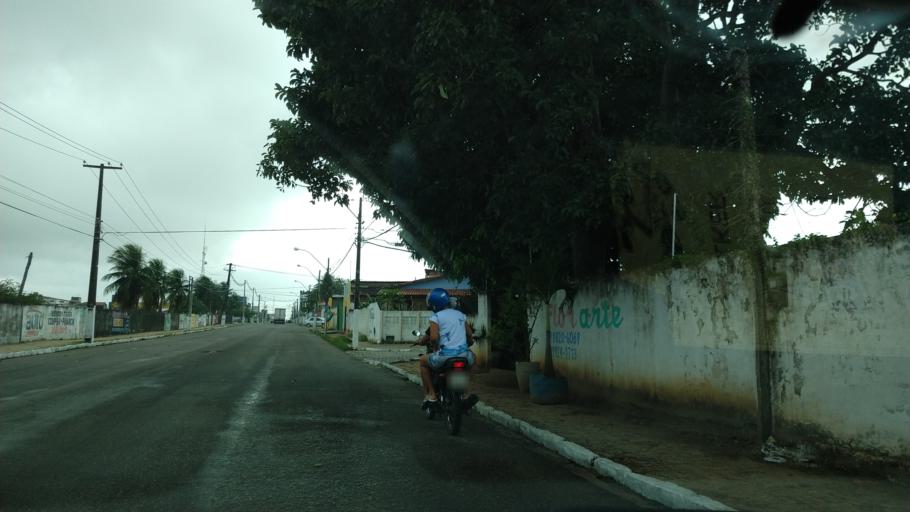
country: BR
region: Rio Grande do Norte
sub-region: Parnamirim
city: Parnamirim
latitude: -5.9246
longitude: -35.2705
